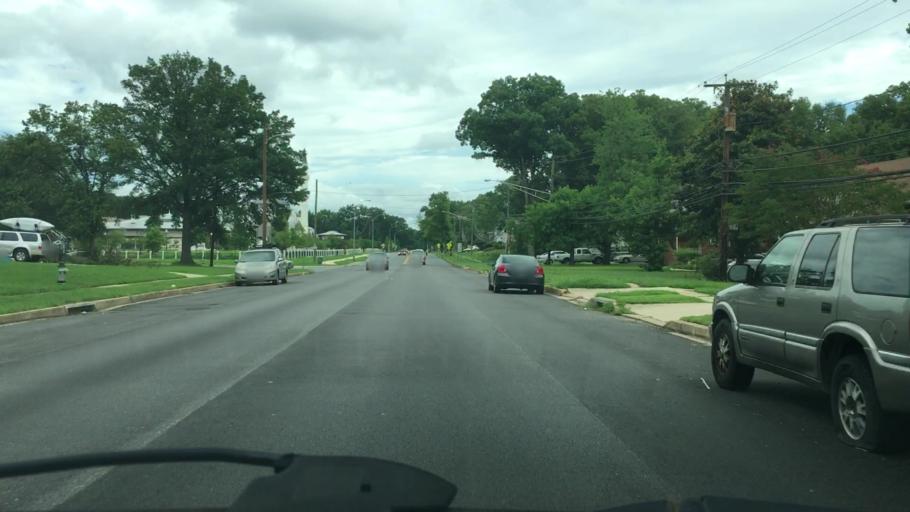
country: US
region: Maryland
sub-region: Prince George's County
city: Goddard
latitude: 38.9811
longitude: -76.8463
